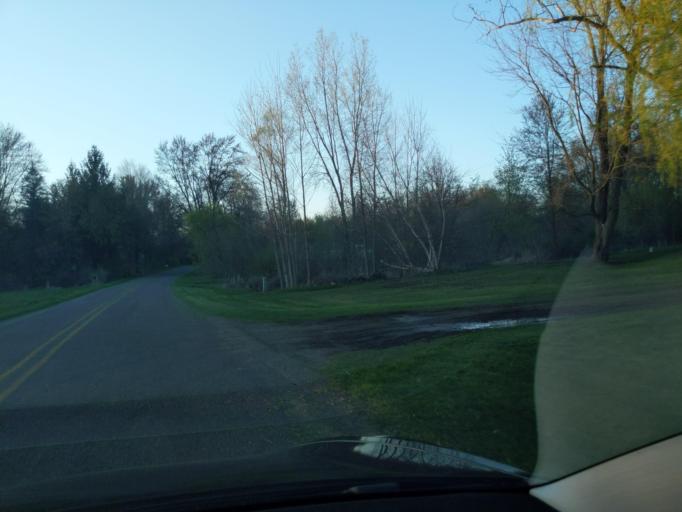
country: US
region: Michigan
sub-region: Ingham County
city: Stockbridge
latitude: 42.4950
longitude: -84.2947
